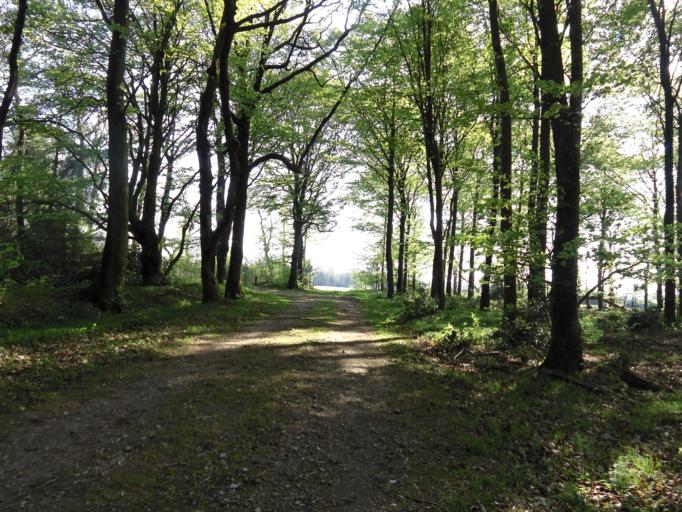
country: DK
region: South Denmark
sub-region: Tonder Kommune
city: Toftlund
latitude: 55.1969
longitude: 8.9378
